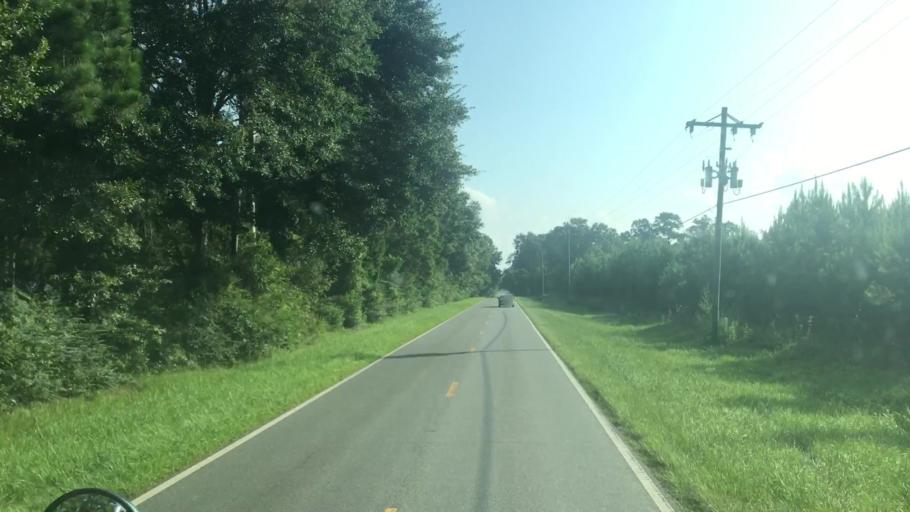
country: US
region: Florida
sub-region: Gadsden County
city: Quincy
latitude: 30.6416
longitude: -84.5742
